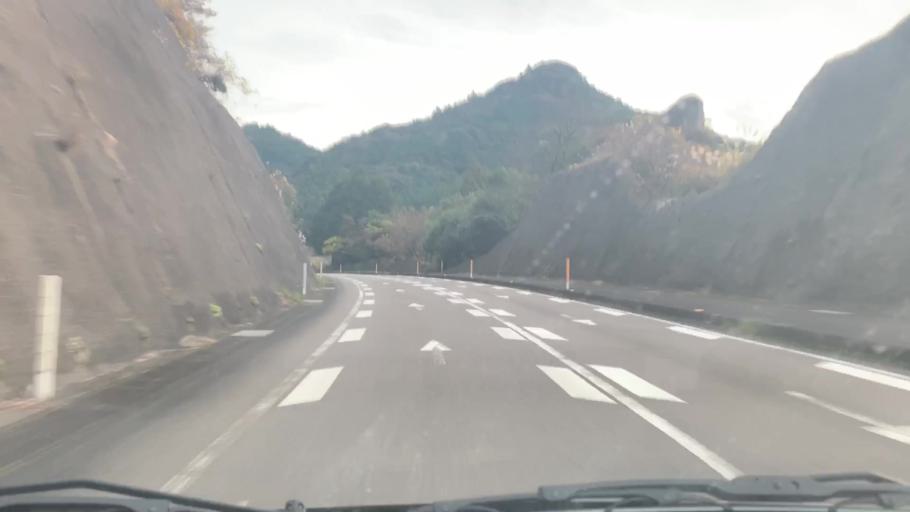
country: JP
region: Saga Prefecture
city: Kashima
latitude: 33.0518
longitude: 130.0727
